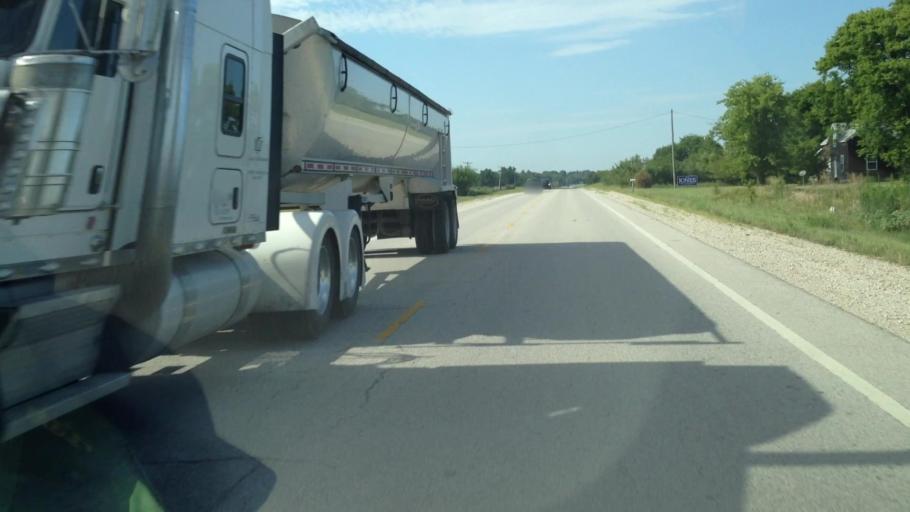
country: US
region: Kansas
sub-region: Neosho County
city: Erie
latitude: 37.5222
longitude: -95.2701
